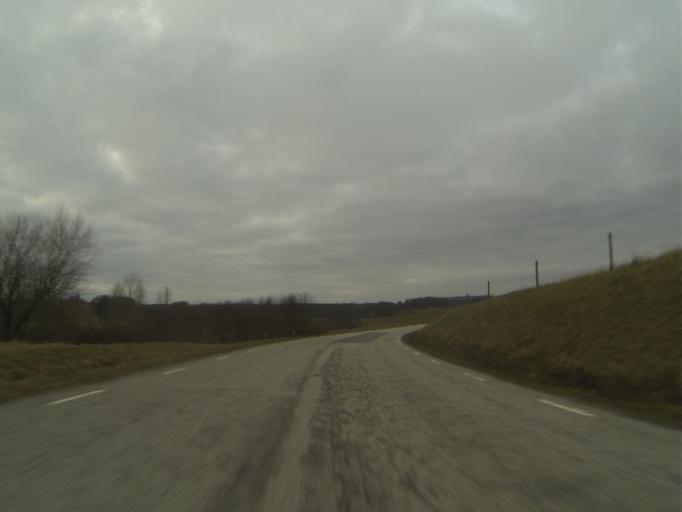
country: SE
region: Skane
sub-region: Skurups Kommun
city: Skurup
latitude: 55.5194
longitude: 13.4402
